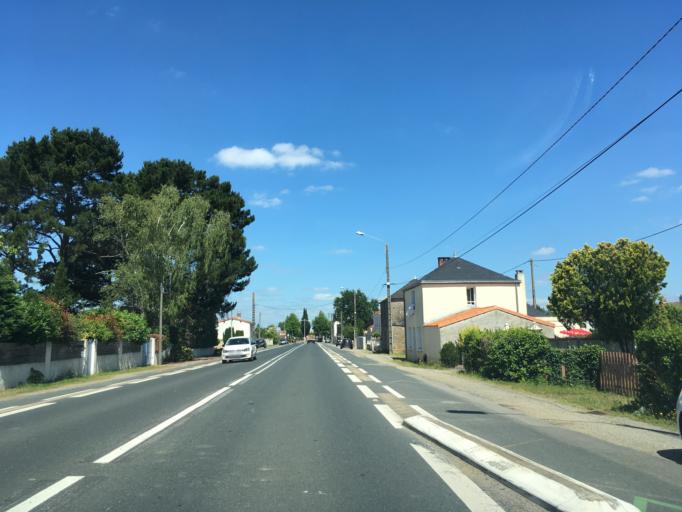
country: FR
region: Pays de la Loire
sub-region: Departement de la Loire-Atlantique
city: Les Sorinieres
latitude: 47.1441
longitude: -1.5259
